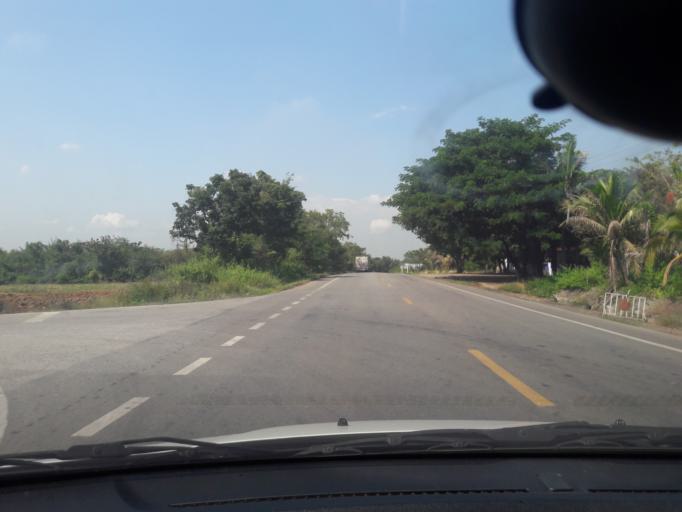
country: TH
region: Lampang
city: Mae Tha
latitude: 18.1886
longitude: 99.5308
